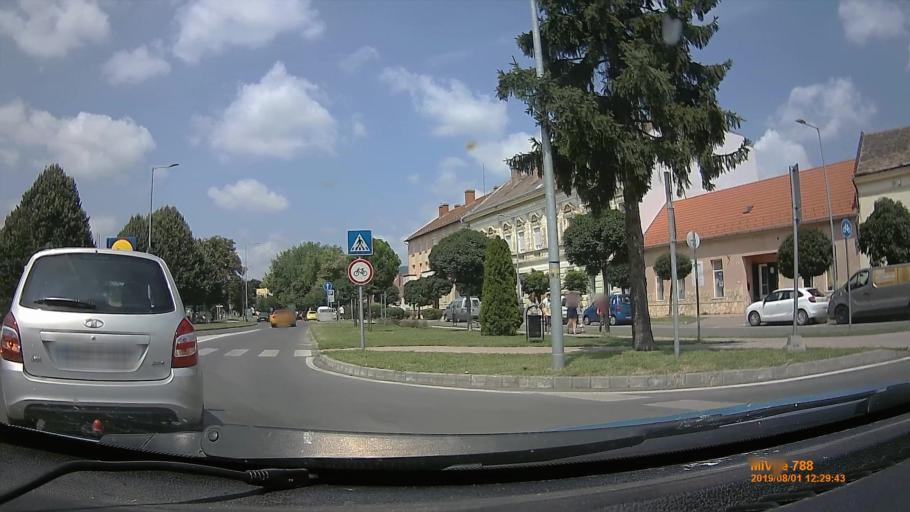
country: HU
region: Baranya
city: Siklos
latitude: 45.8561
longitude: 18.2947
